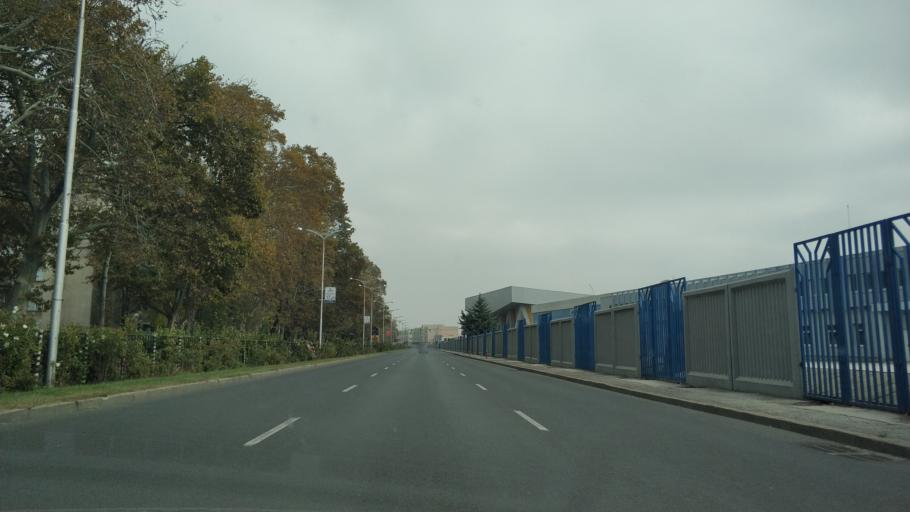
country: BG
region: Plovdiv
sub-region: Obshtina Plovdiv
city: Plovdiv
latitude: 42.1592
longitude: 24.7525
